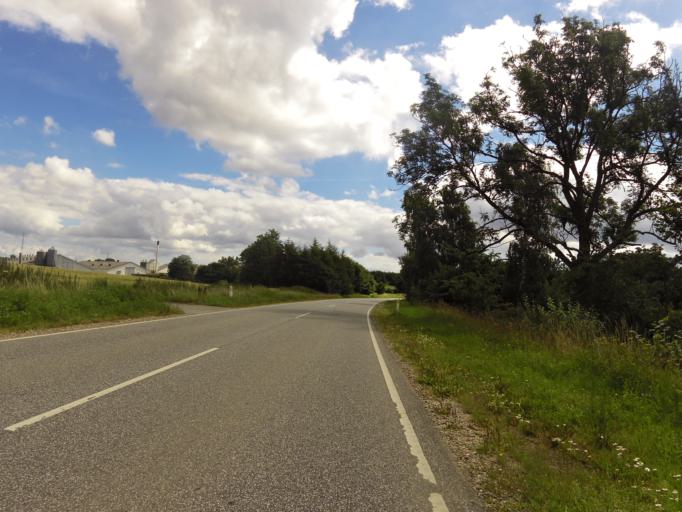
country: DK
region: South Denmark
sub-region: Haderslev Kommune
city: Haderslev
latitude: 55.2765
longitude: 9.4198
